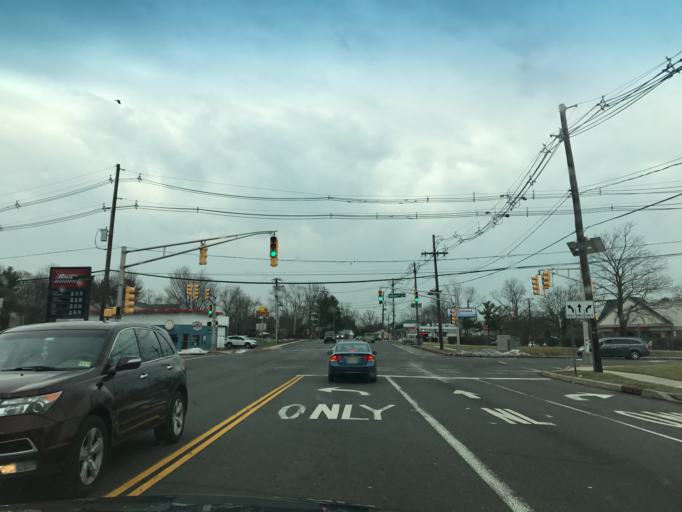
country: US
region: New Jersey
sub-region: Middlesex County
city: East Brunswick
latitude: 40.4369
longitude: -74.4228
